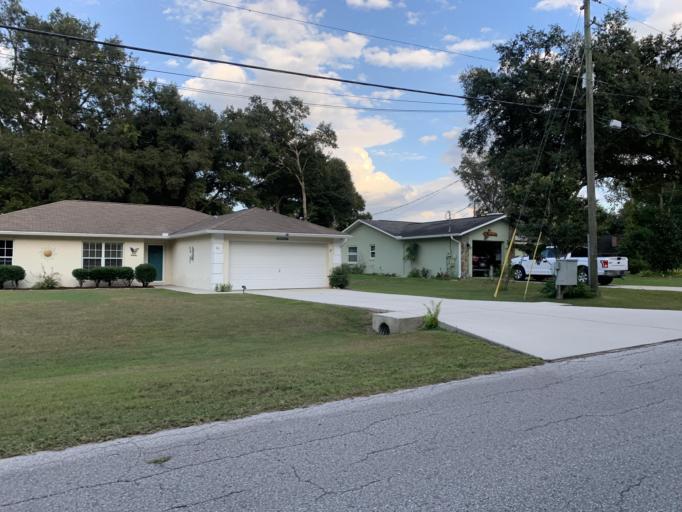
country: US
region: Florida
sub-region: Marion County
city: Silver Springs Shores
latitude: 29.1644
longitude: -82.0458
